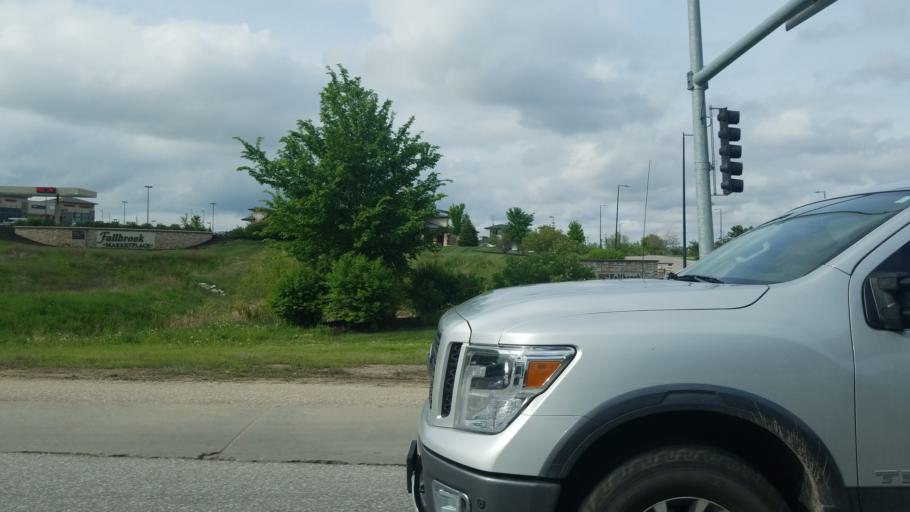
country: US
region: Nebraska
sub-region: Lancaster County
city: Lincoln
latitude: 40.8758
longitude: -96.7342
